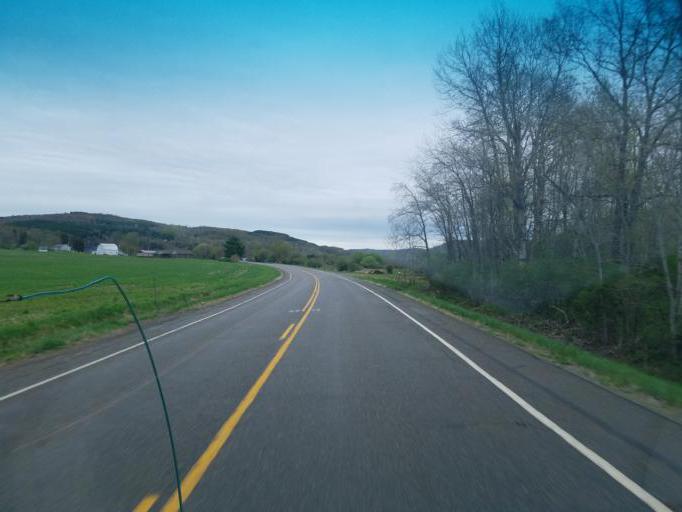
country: US
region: New York
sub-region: Allegany County
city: Andover
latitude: 42.0332
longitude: -77.7854
